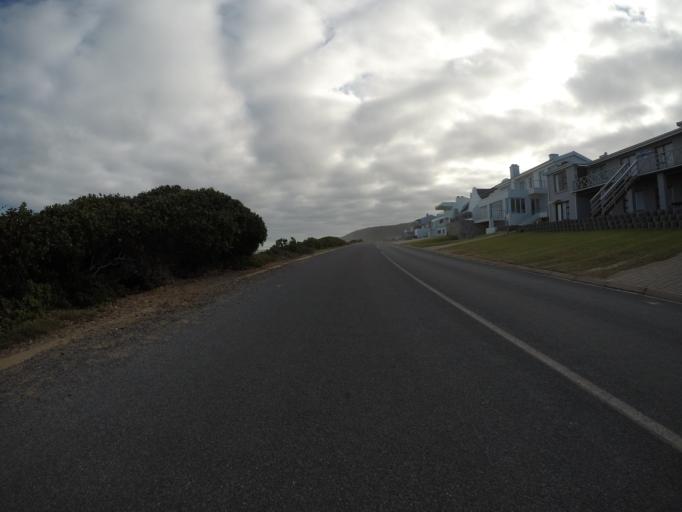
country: ZA
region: Western Cape
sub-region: Eden District Municipality
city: Riversdale
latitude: -34.4329
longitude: 21.3328
